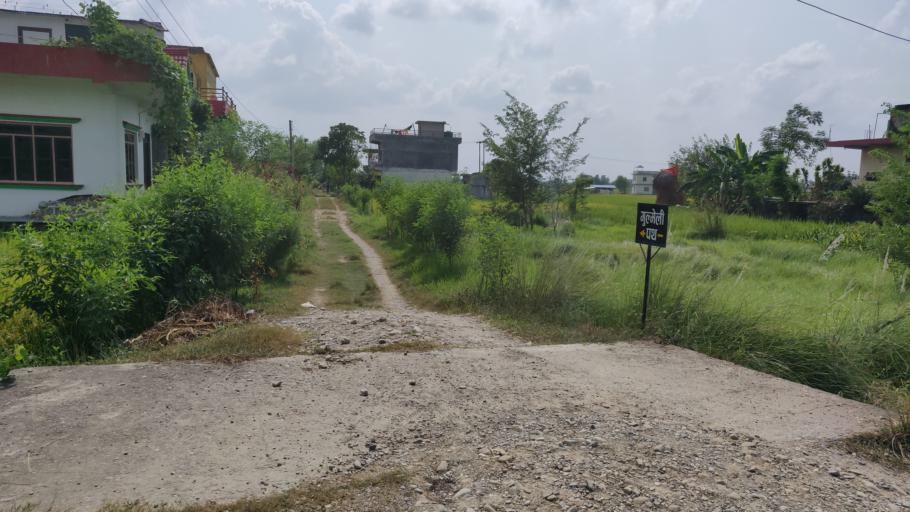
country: NP
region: Western Region
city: Butwal
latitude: 27.6065
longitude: 83.4890
